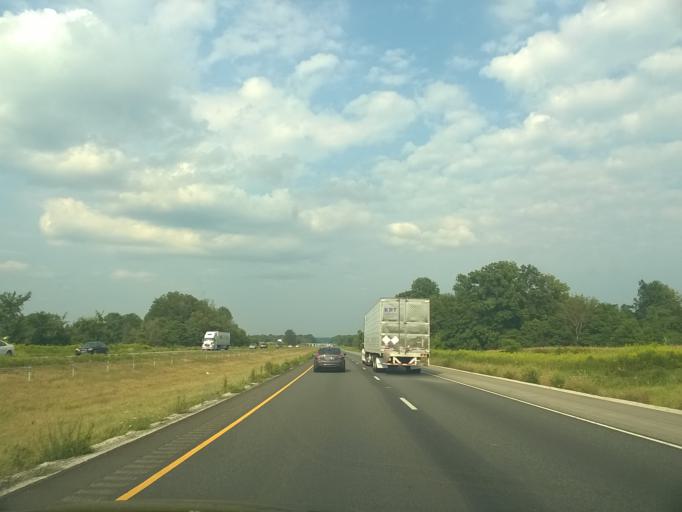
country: US
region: Indiana
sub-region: Clay County
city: Brazil
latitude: 39.4722
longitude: -87.0254
